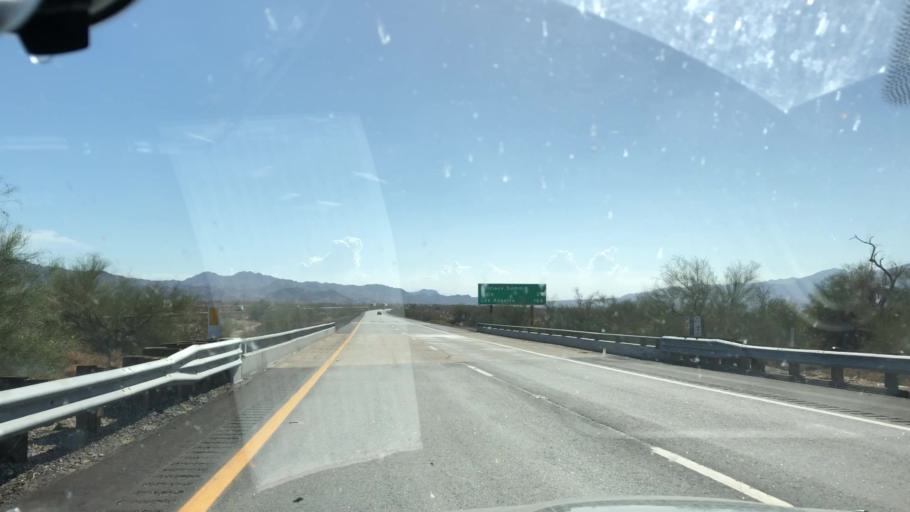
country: US
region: California
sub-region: Imperial County
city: Niland
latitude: 33.6753
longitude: -115.5741
